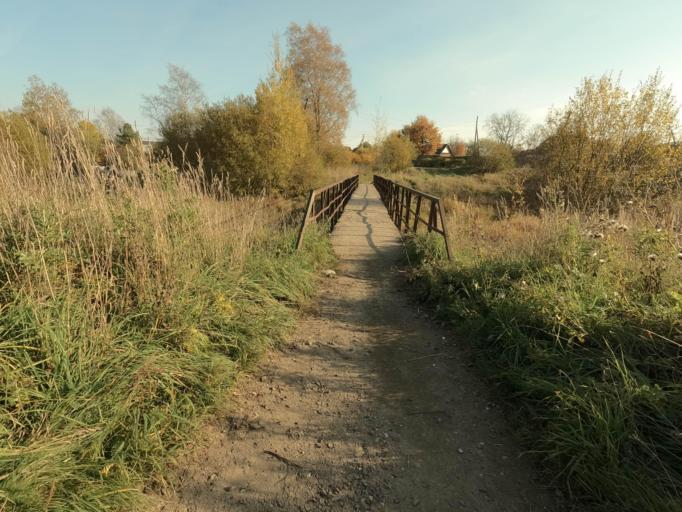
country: RU
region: Leningrad
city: Mga
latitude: 59.7532
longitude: 31.0612
